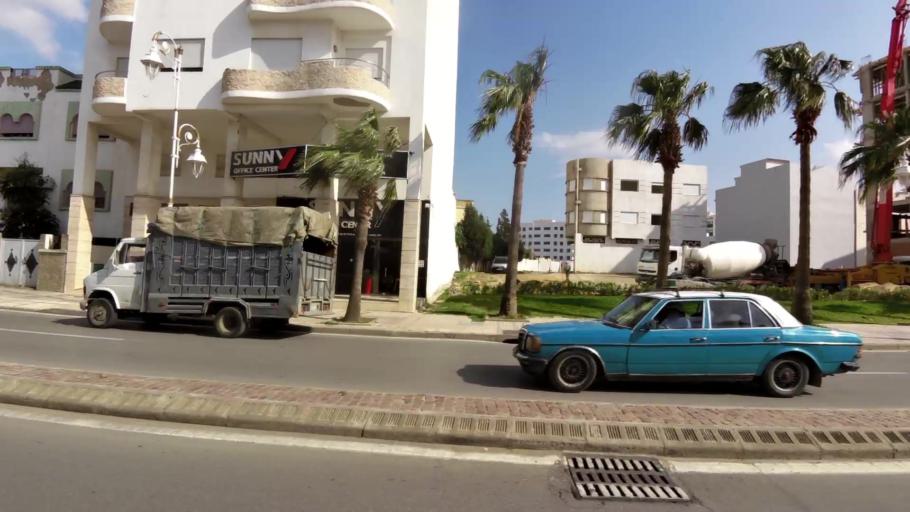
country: MA
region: Tanger-Tetouan
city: Tetouan
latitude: 35.5913
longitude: -5.3445
